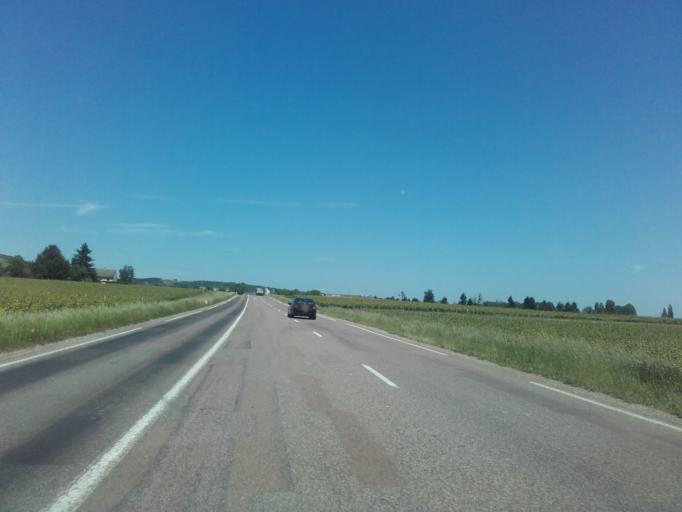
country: FR
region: Bourgogne
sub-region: Departement de la Cote-d'Or
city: Beaune
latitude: 47.0602
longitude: 4.8633
